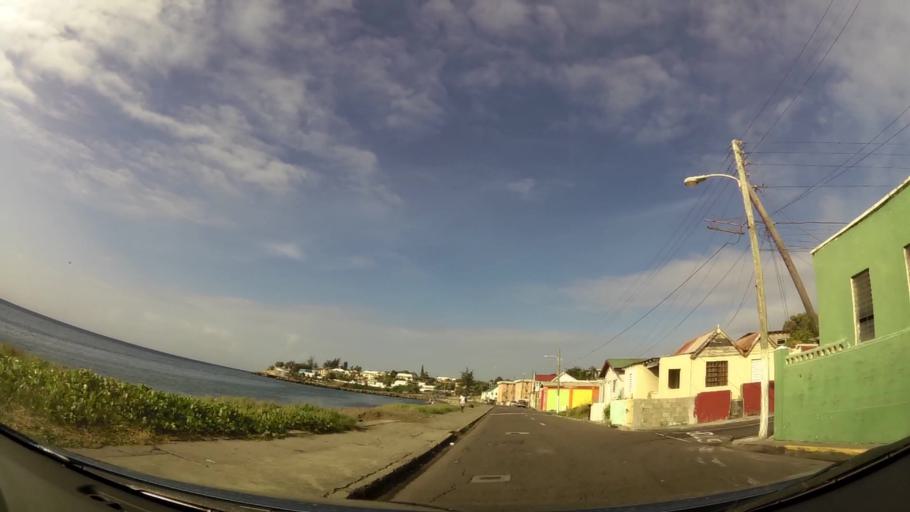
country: KN
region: Saint George Basseterre
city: Basseterre
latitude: 17.2936
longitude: -62.7288
